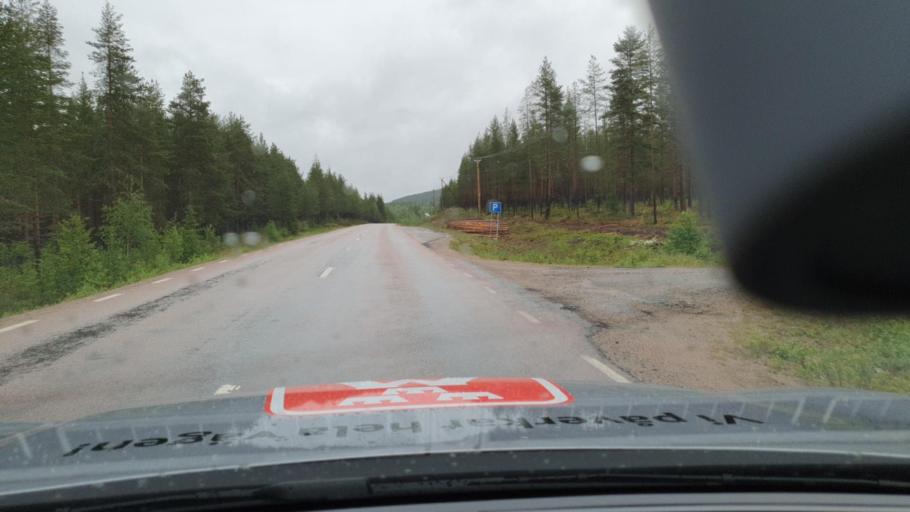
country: SE
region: Norrbotten
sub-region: Overkalix Kommun
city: OEverkalix
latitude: 66.4066
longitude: 22.9553
